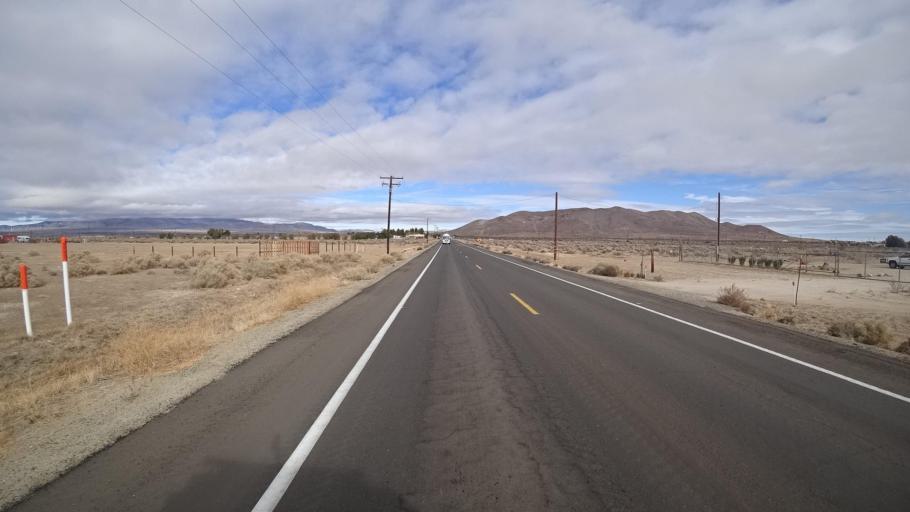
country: US
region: California
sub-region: Kern County
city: Rosamond
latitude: 34.8607
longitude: -118.2910
